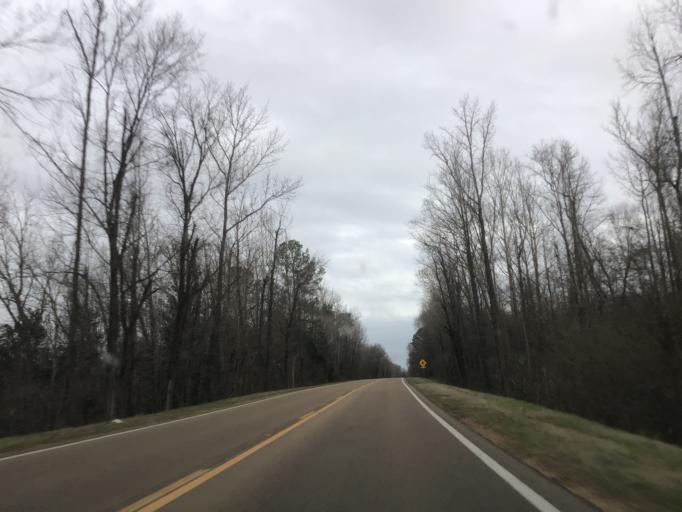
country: US
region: Mississippi
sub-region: Warren County
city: Beechwood
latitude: 32.3069
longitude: -90.8039
